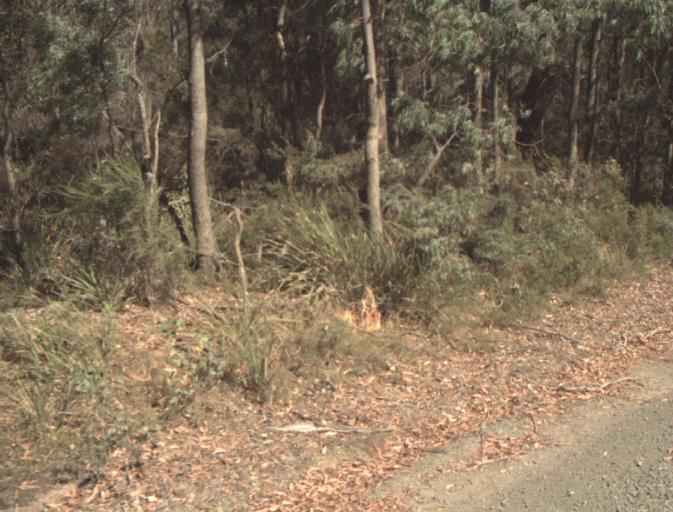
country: AU
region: Tasmania
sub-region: Launceston
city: Mayfield
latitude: -41.3499
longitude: 147.2186
